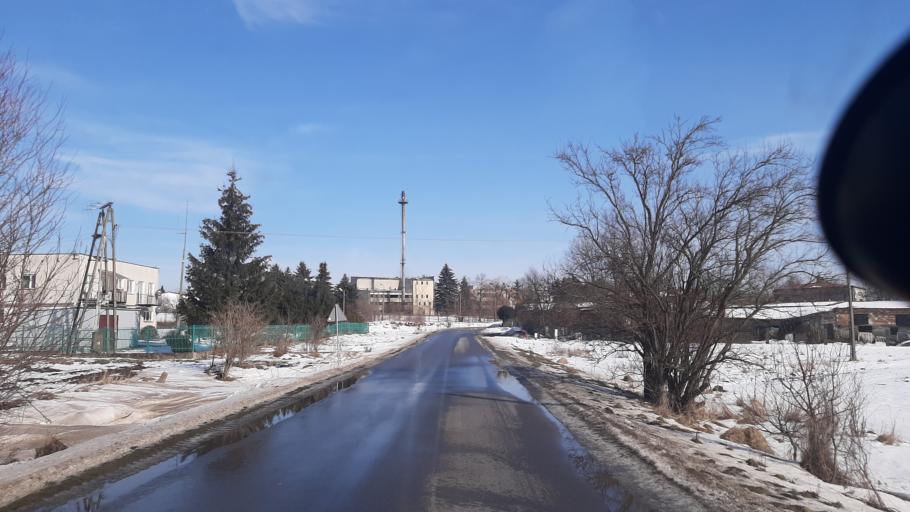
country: PL
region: Lublin Voivodeship
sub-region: Powiat pulawski
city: Kurow
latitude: 51.3846
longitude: 22.1672
